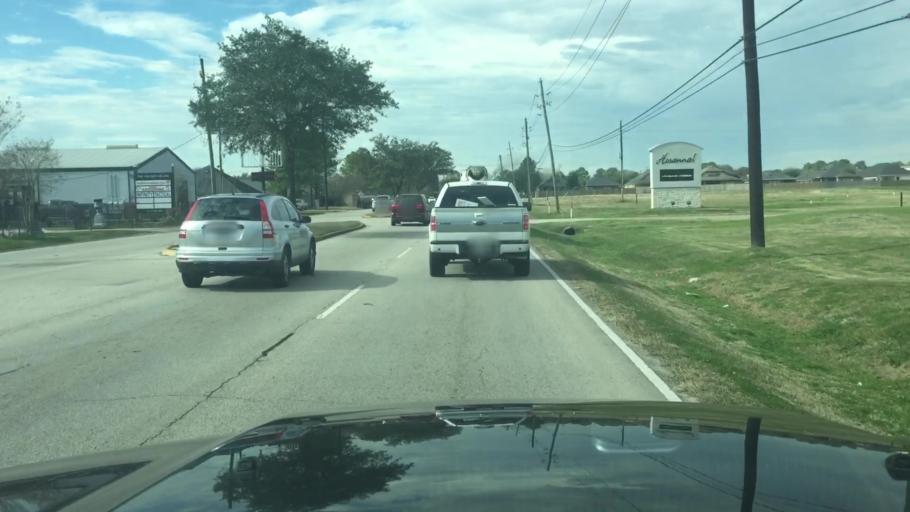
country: US
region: Texas
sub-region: Harris County
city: Oak Cliff Place
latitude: 29.8311
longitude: -95.6700
